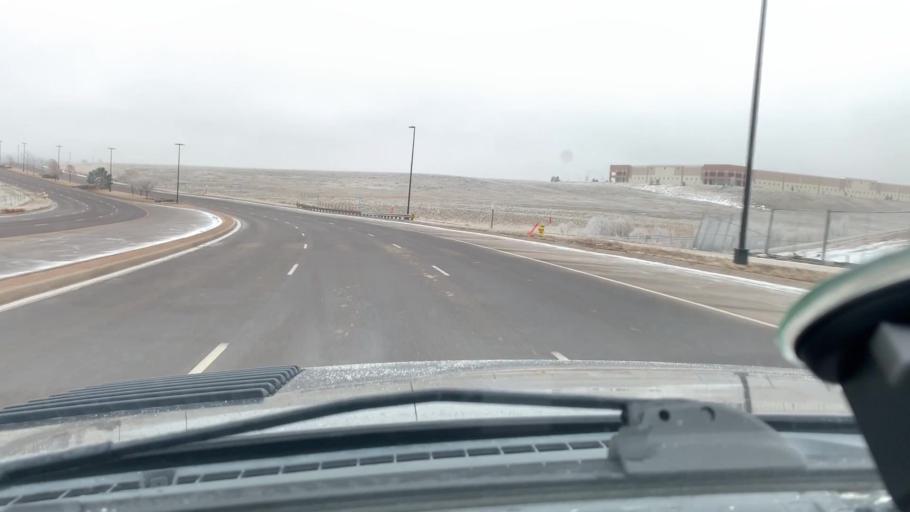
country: US
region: Colorado
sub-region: Arapahoe County
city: Dove Valley
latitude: 39.5766
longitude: -104.8192
